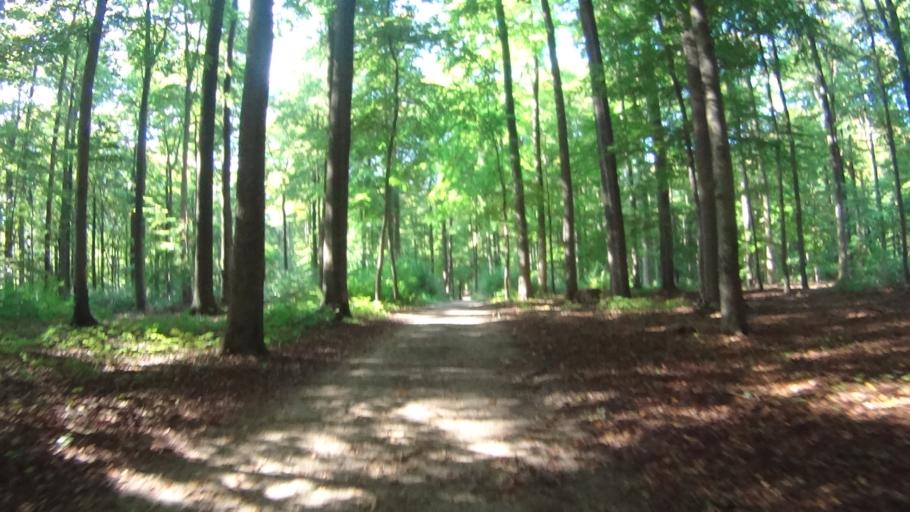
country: BE
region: Flanders
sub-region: Provincie Vlaams-Brabant
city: Hoeilaart
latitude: 50.7921
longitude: 4.4550
